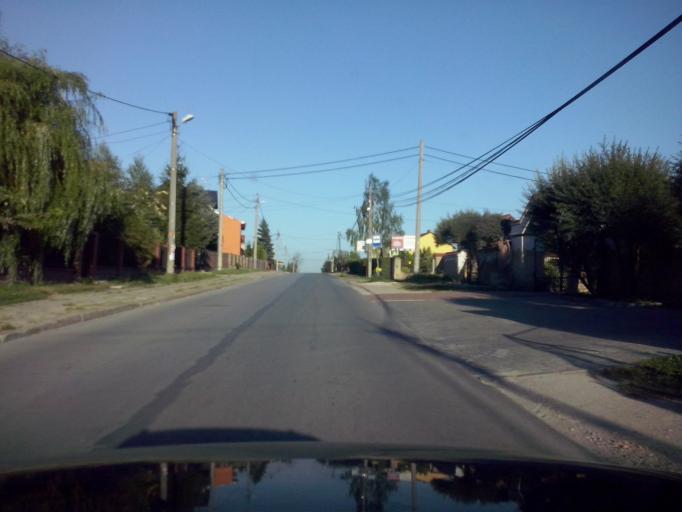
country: PL
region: Swietokrzyskie
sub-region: Powiat kielecki
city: Kielce
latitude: 50.8188
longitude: 20.6282
